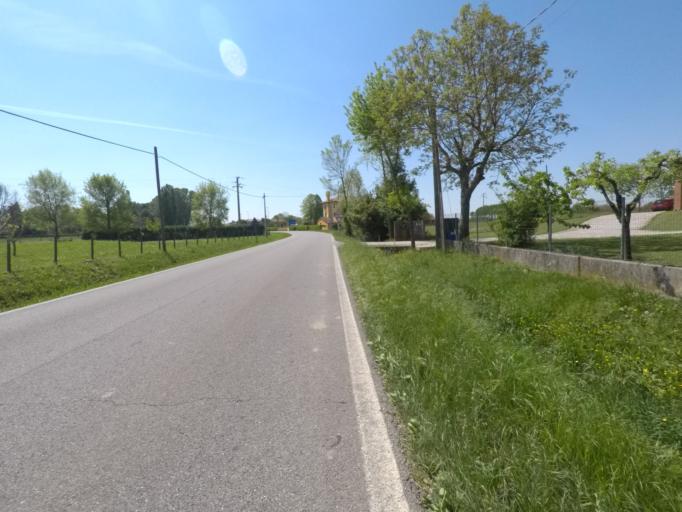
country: IT
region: Veneto
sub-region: Provincia di Treviso
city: Mansue
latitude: 45.8194
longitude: 12.5566
